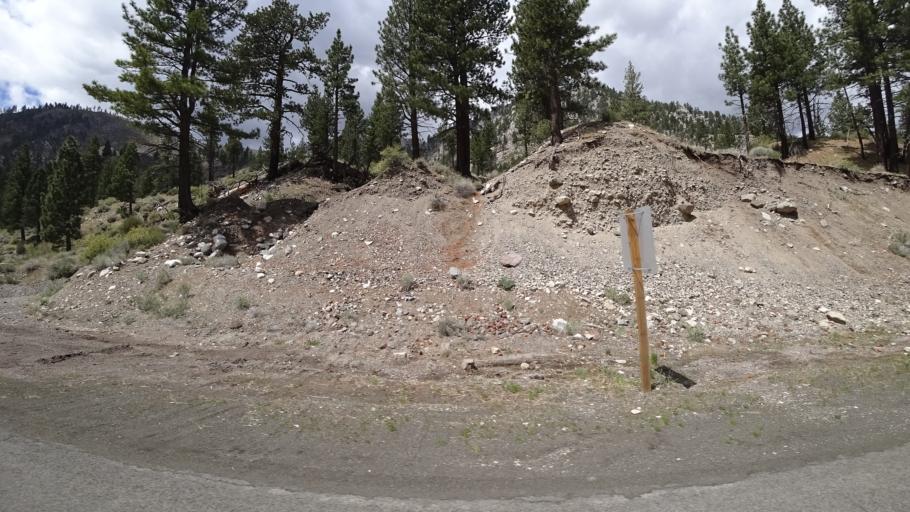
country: US
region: California
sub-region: Mono County
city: Bridgeport
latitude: 38.4371
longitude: -119.4529
